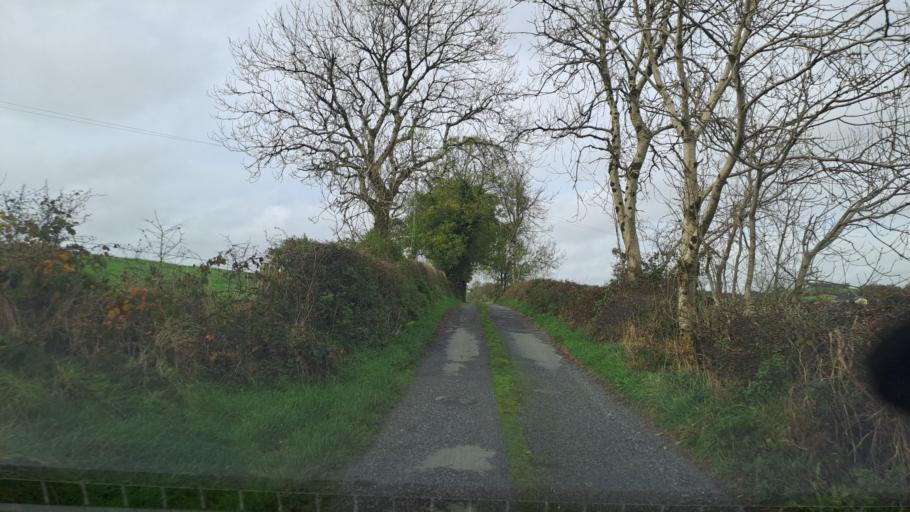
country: IE
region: Ulster
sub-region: County Monaghan
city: Carrickmacross
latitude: 54.0100
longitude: -6.7959
